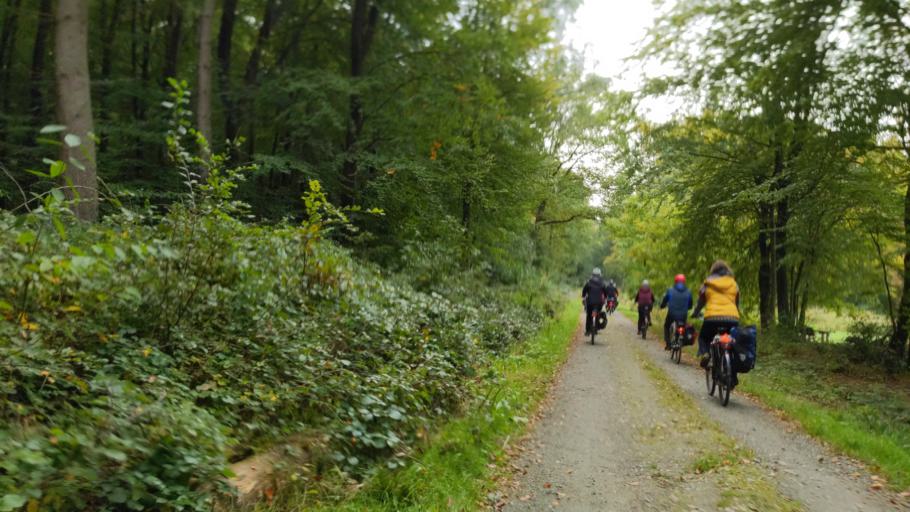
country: DE
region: Schleswig-Holstein
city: Rehhorst
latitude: 53.8514
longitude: 10.4650
